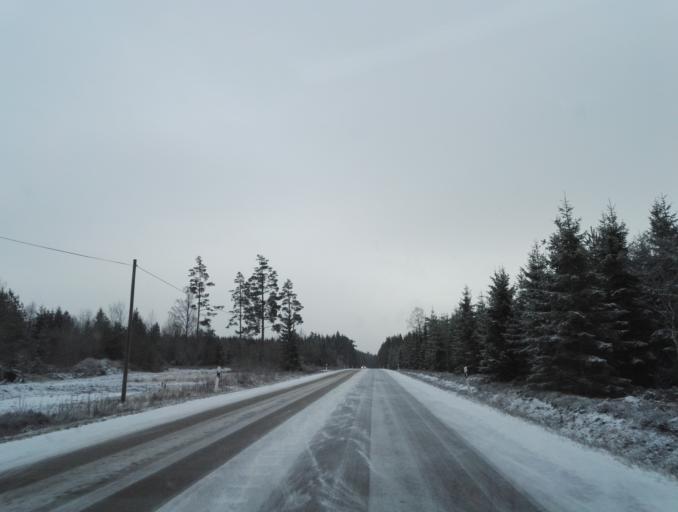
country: SE
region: Kronoberg
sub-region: Uppvidinge Kommun
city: Lenhovda
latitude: 56.9819
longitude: 15.2972
